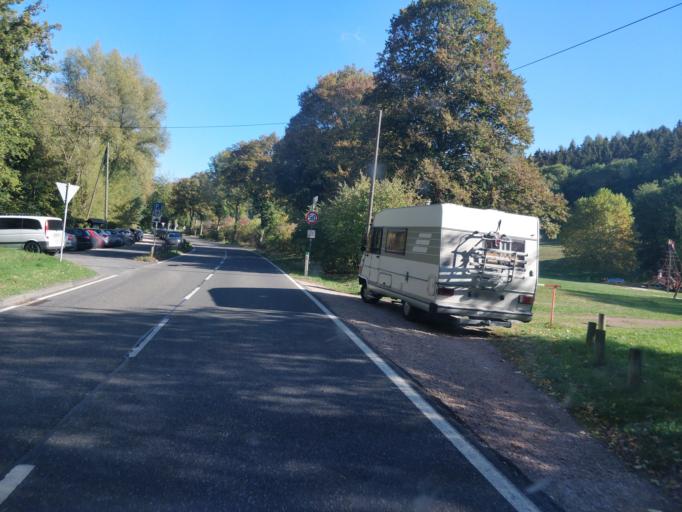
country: DE
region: North Rhine-Westphalia
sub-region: Regierungsbezirk Koln
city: Bad Munstereifel
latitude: 50.5603
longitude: 6.7739
